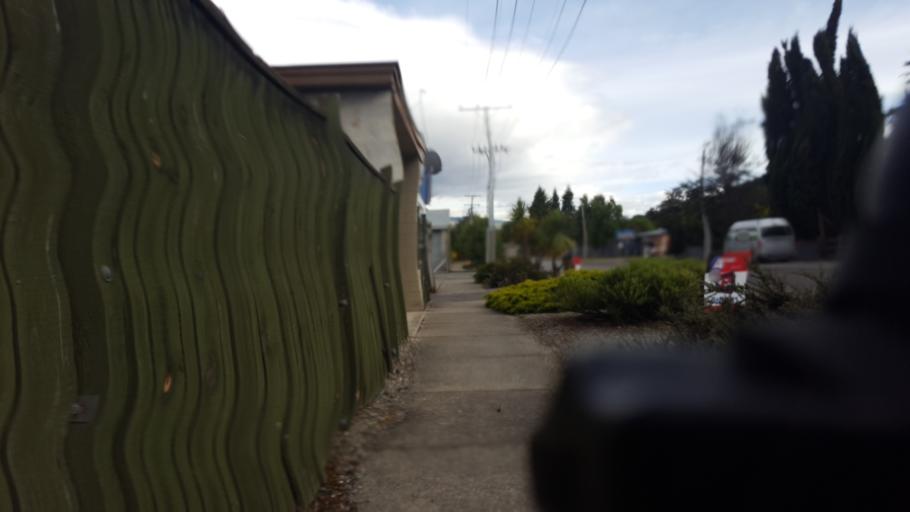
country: NZ
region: Otago
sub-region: Queenstown-Lakes District
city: Wanaka
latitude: -45.2440
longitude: 169.3957
